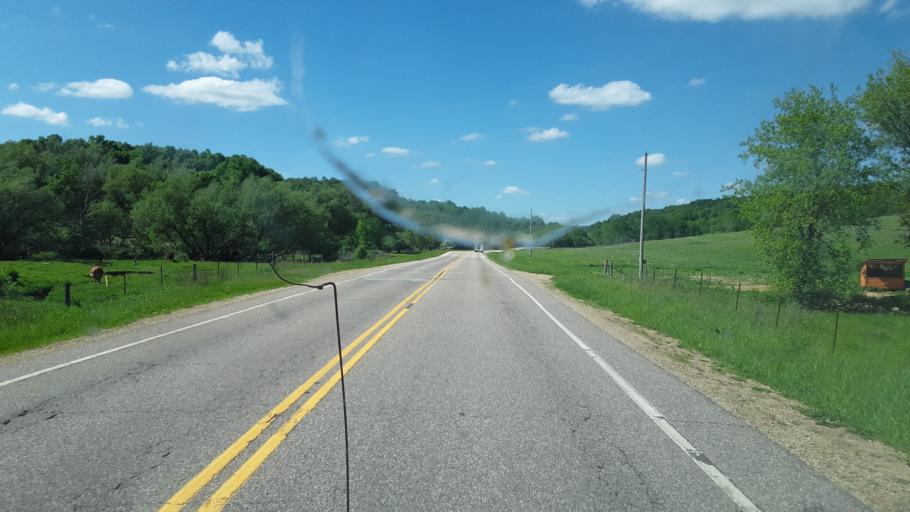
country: US
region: Wisconsin
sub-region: Sauk County
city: Reedsburg
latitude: 43.4991
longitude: -90.2048
